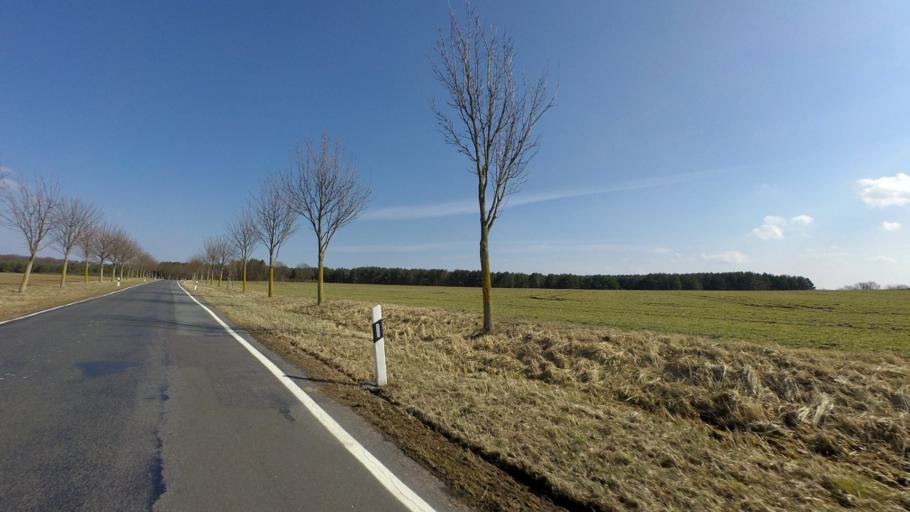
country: DE
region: Brandenburg
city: Wiesenburg
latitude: 52.0857
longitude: 12.4575
